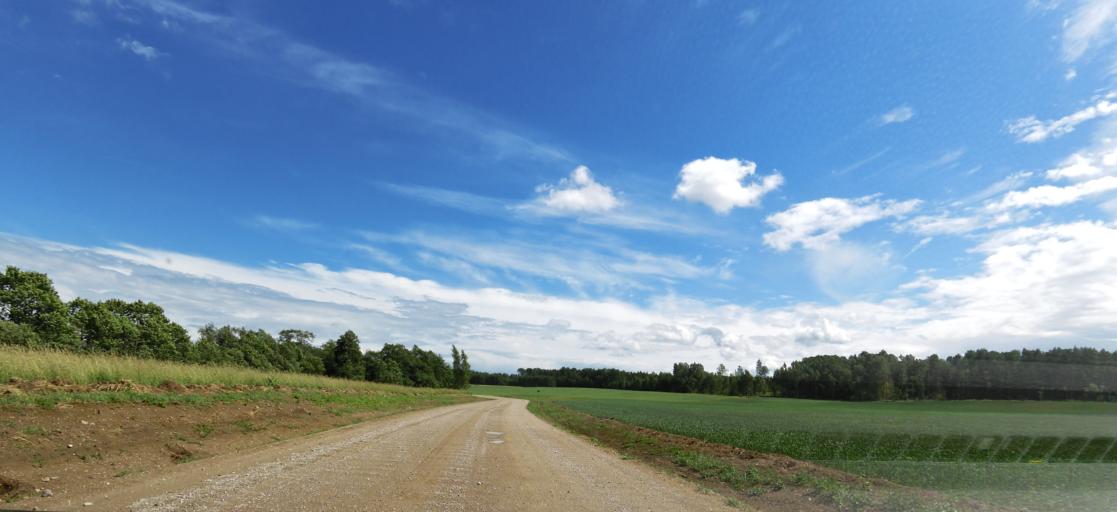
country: LT
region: Panevezys
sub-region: Birzai
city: Birzai
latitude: 56.4106
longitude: 24.8218
